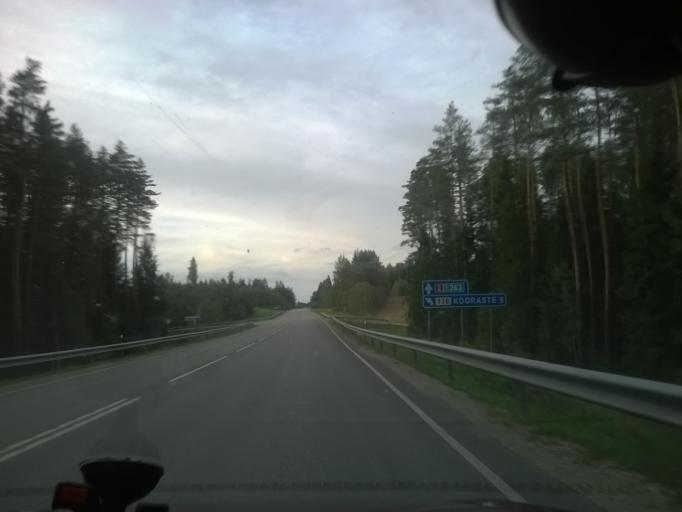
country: EE
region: Vorumaa
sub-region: Voru linn
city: Voru
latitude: 57.9704
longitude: 26.7855
